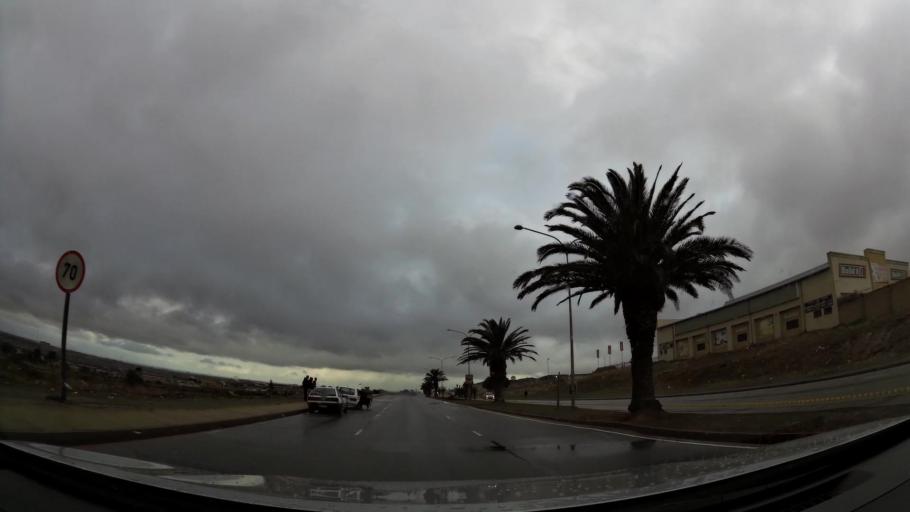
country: ZA
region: Eastern Cape
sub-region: Nelson Mandela Bay Metropolitan Municipality
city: Port Elizabeth
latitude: -33.8923
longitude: 25.5252
